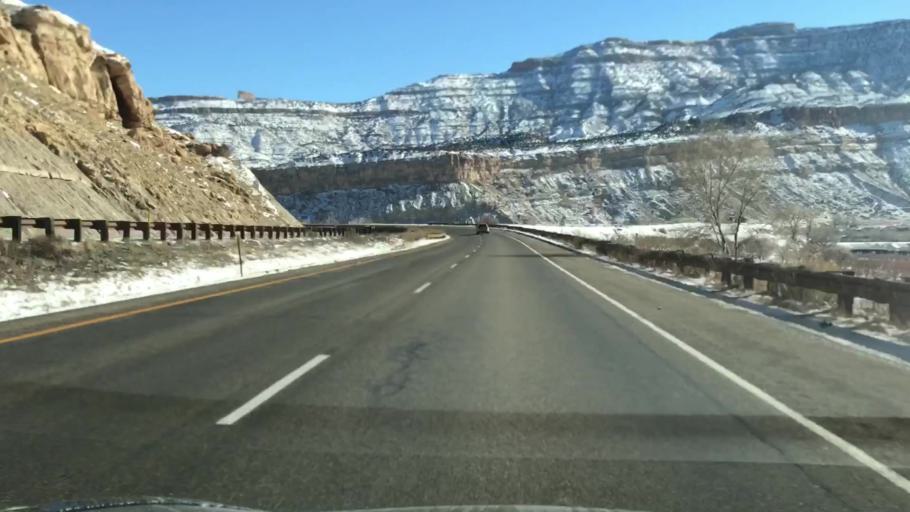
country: US
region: Colorado
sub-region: Mesa County
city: Palisade
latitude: 39.1182
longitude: -108.3331
